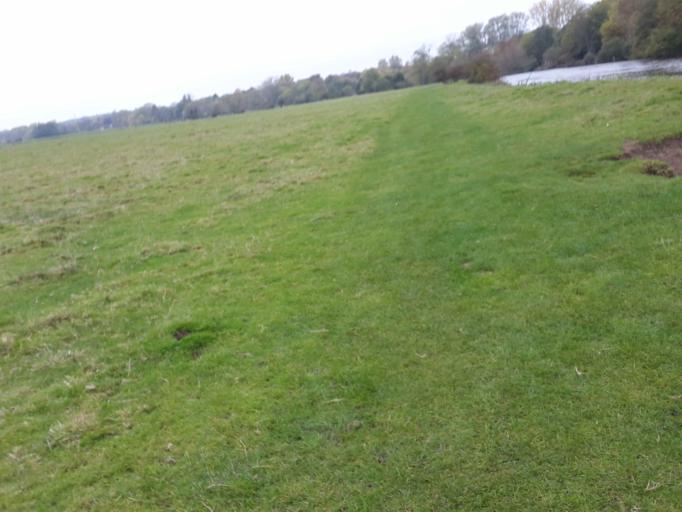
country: GB
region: England
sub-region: Oxfordshire
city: Radley
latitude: 51.6536
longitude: -1.1810
